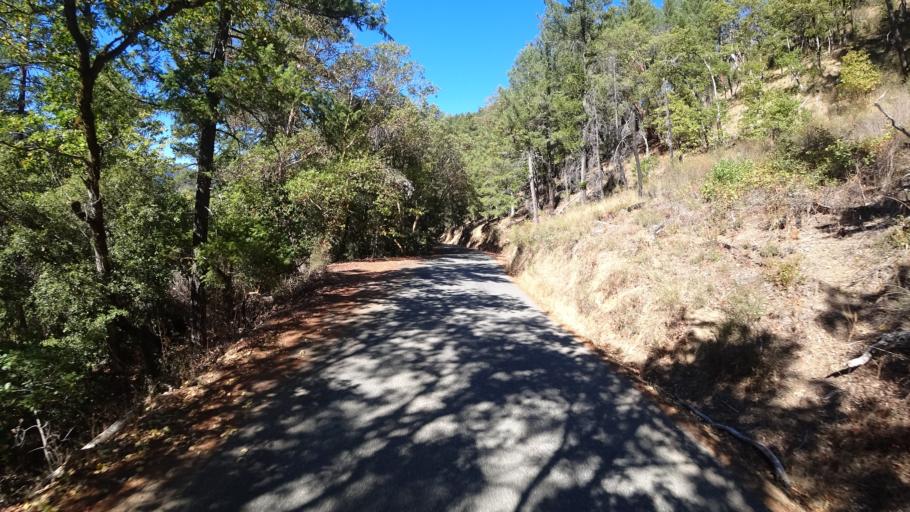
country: US
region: California
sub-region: Humboldt County
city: Willow Creek
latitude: 41.2814
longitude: -123.3504
